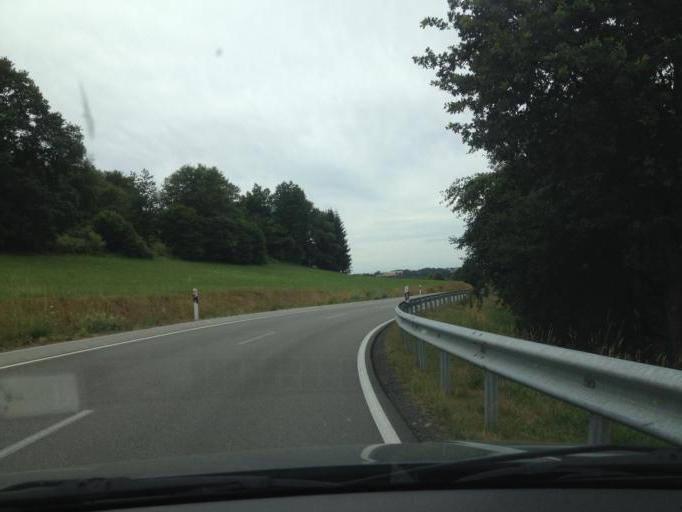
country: DE
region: Rheinland-Pfalz
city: Geiselberg
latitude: 49.3250
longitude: 7.6857
